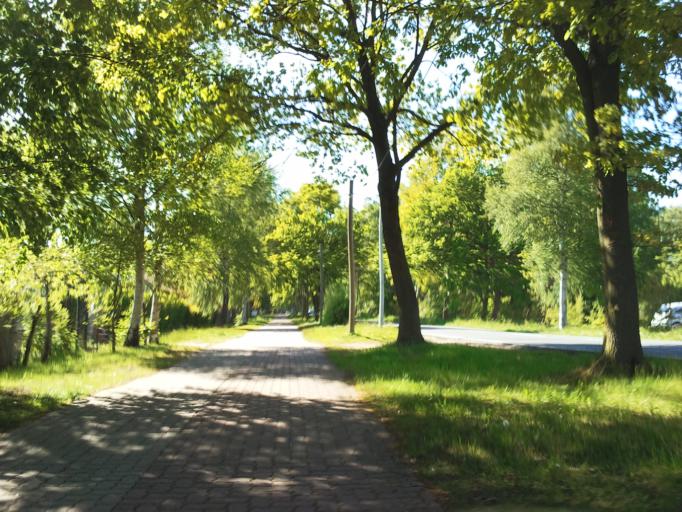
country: DE
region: Mecklenburg-Vorpommern
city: Nienhagen
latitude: 54.1913
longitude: 12.1534
